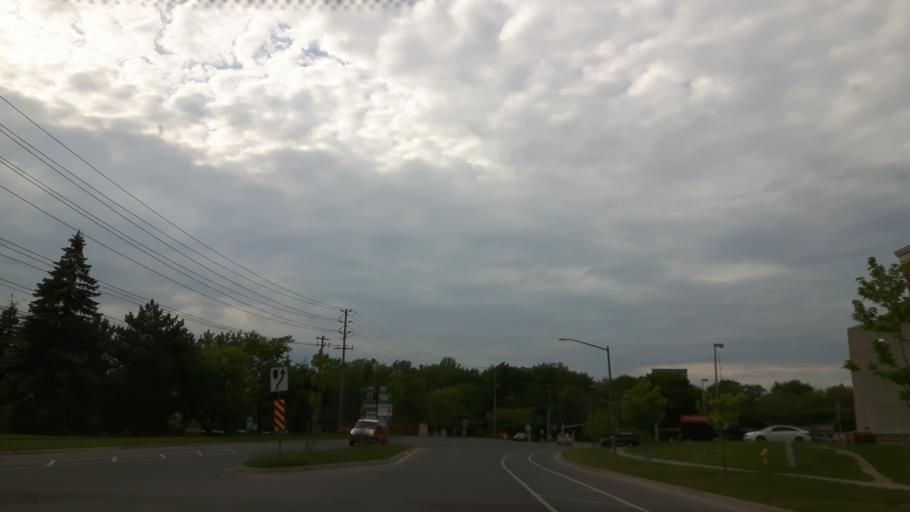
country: CA
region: Ontario
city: London
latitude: 42.9427
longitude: -81.2137
